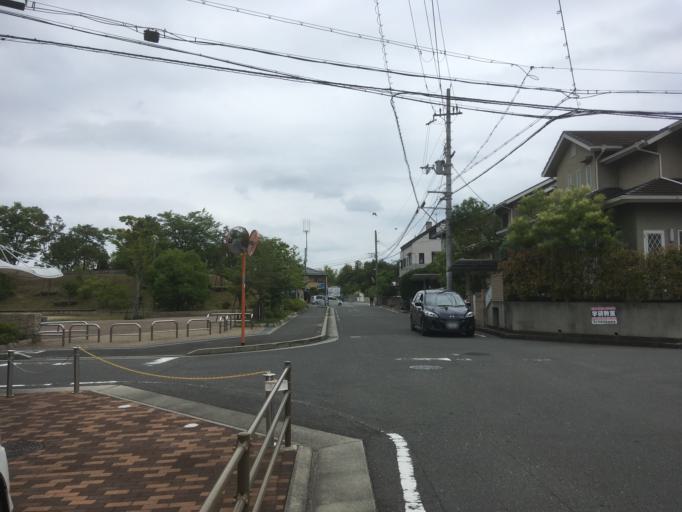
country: JP
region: Nara
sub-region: Ikoma-shi
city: Ikoma
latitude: 34.7206
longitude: 135.7175
